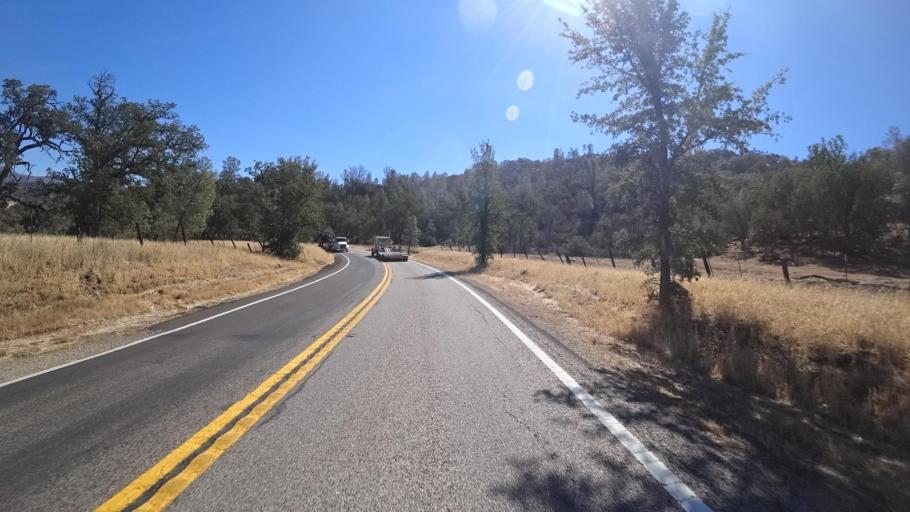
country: US
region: California
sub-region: Fresno County
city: Coalinga
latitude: 36.1965
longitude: -120.7202
